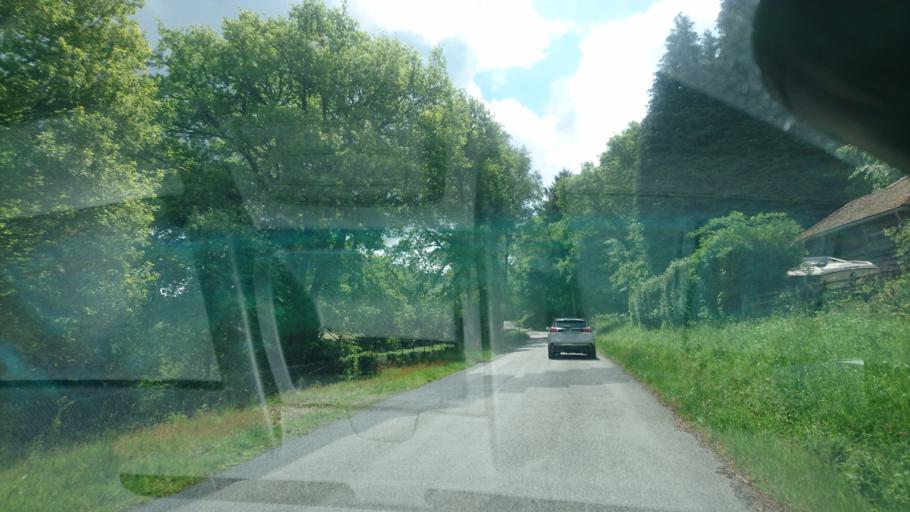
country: FR
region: Limousin
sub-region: Departement de la Haute-Vienne
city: Peyrat-le-Chateau
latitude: 45.7883
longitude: 1.8991
